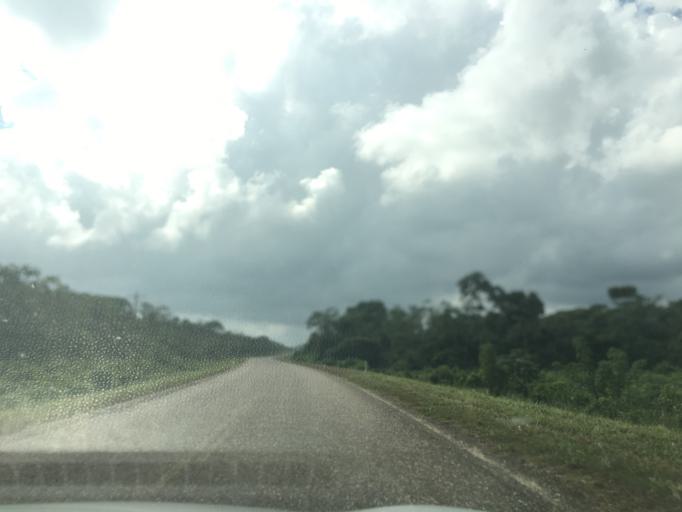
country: BZ
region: Stann Creek
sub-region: Dangriga
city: Dangriga
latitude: 16.9561
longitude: -88.3176
